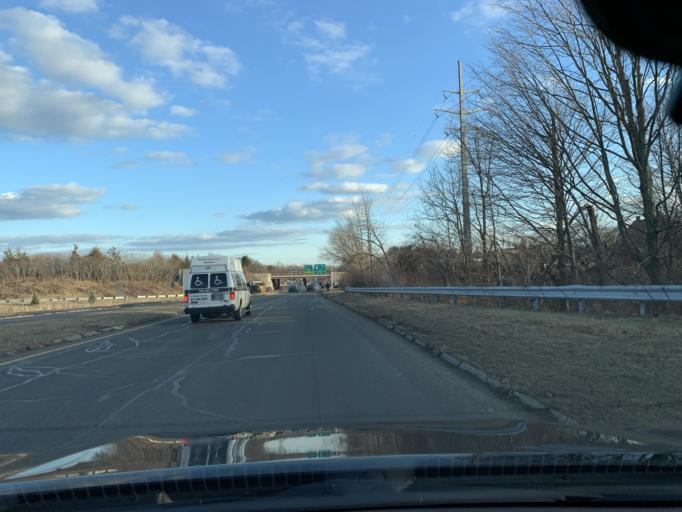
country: US
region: Massachusetts
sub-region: Essex County
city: Danvers
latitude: 42.5853
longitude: -70.9697
